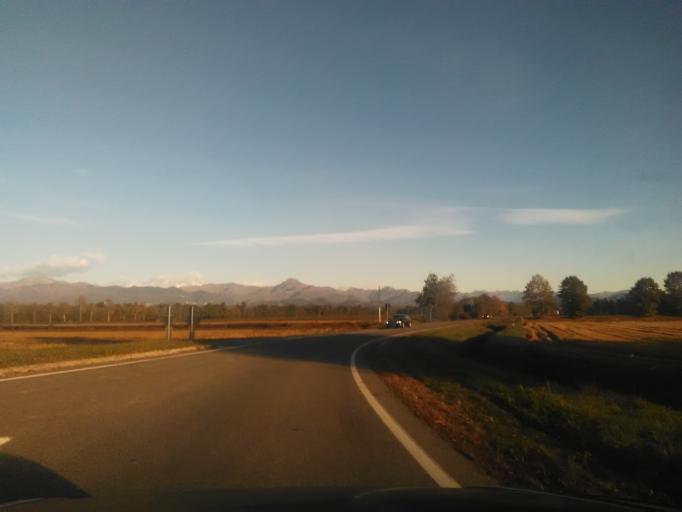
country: IT
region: Piedmont
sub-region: Provincia di Vercelli
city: Rovasenda
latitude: 45.5383
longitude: 8.3030
